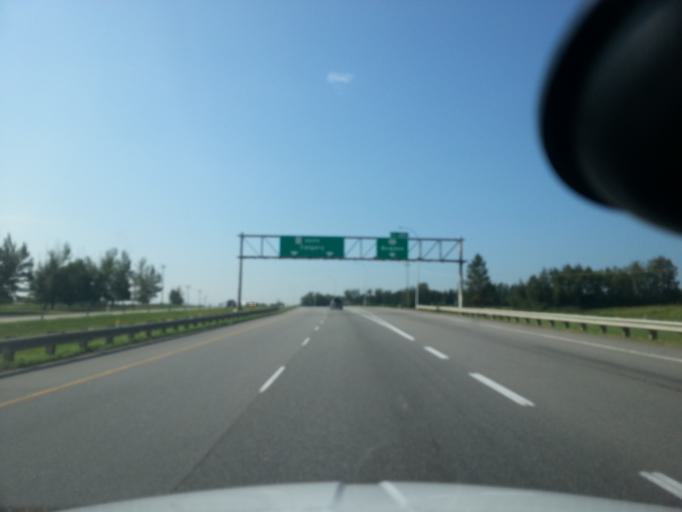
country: CA
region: Alberta
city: Olds
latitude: 51.9466
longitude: -114.0242
